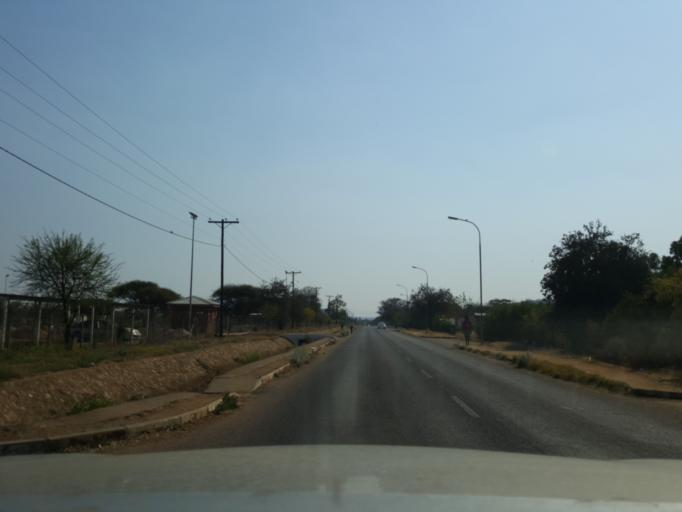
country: BW
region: South East
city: Lobatse
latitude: -25.2000
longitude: 25.6899
